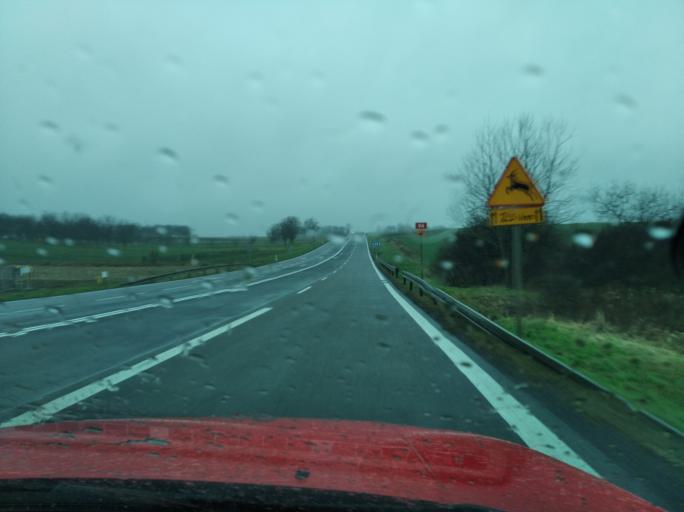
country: PL
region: Subcarpathian Voivodeship
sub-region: Powiat przeworski
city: Nowosielce
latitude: 50.0654
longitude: 22.4122
